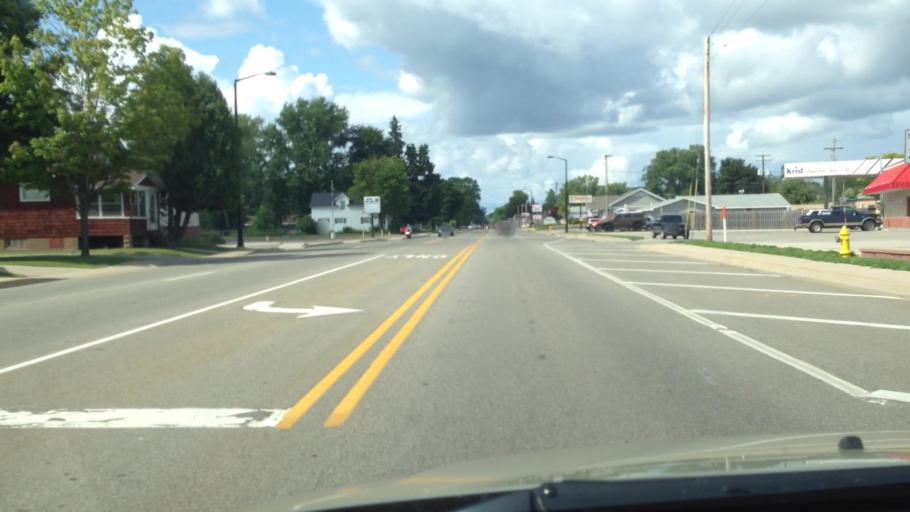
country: US
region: Michigan
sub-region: Menominee County
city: Menominee
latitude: 45.1346
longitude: -87.6125
